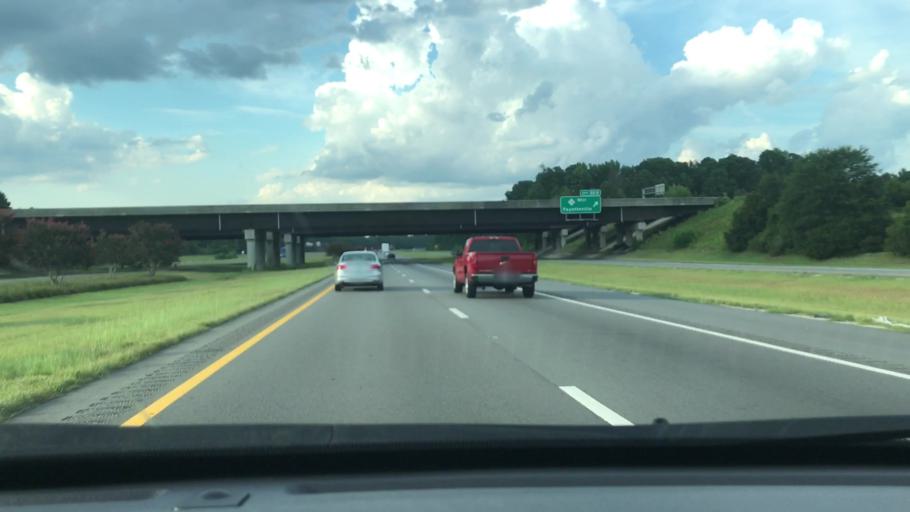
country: US
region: North Carolina
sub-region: Cumberland County
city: Vander
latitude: 35.0415
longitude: -78.8036
